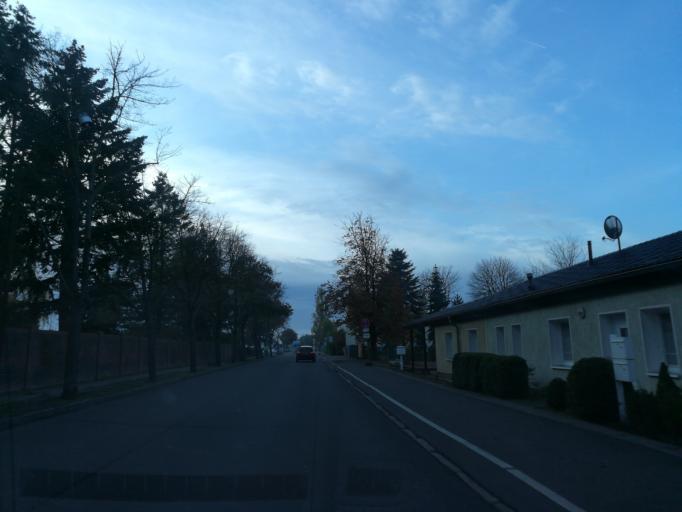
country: DE
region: Saxony-Anhalt
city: Haldensleben I
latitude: 52.2821
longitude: 11.4219
